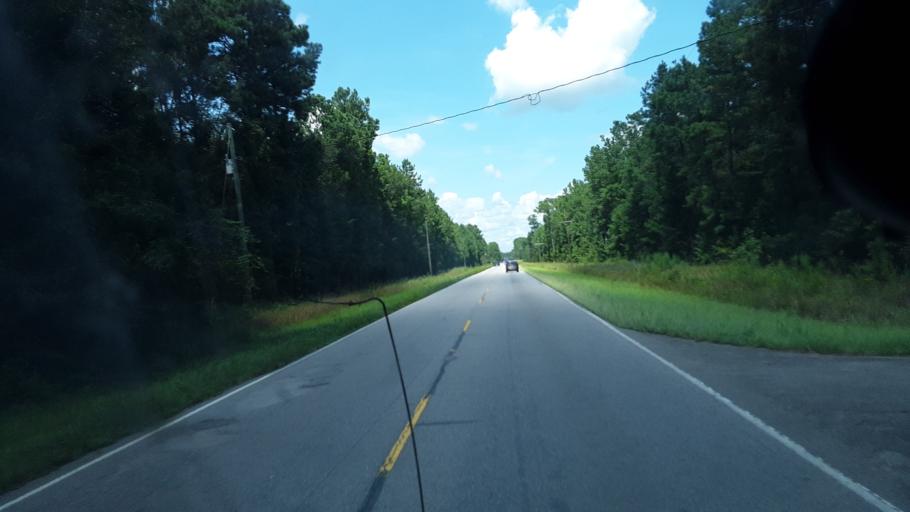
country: US
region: South Carolina
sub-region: Williamsburg County
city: Andrews
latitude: 33.3330
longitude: -79.6627
